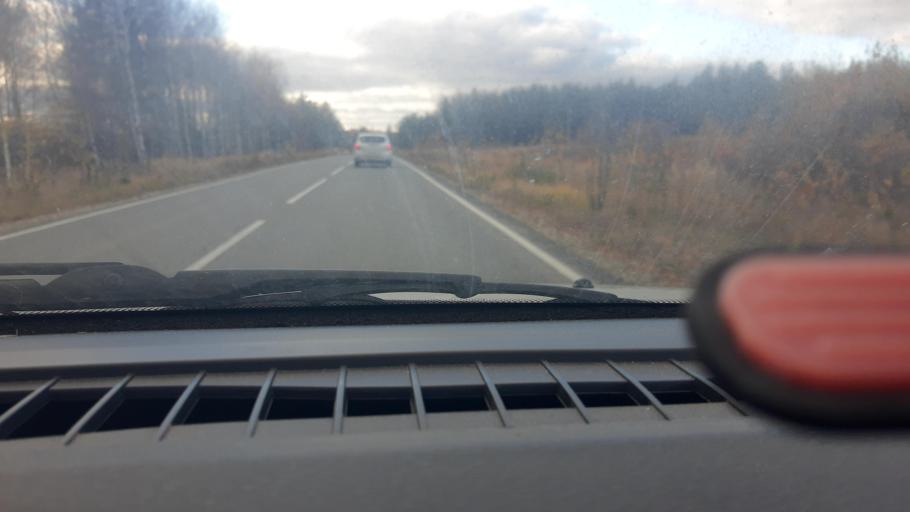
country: RU
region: Nizjnij Novgorod
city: Babino
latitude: 56.2969
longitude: 43.6052
